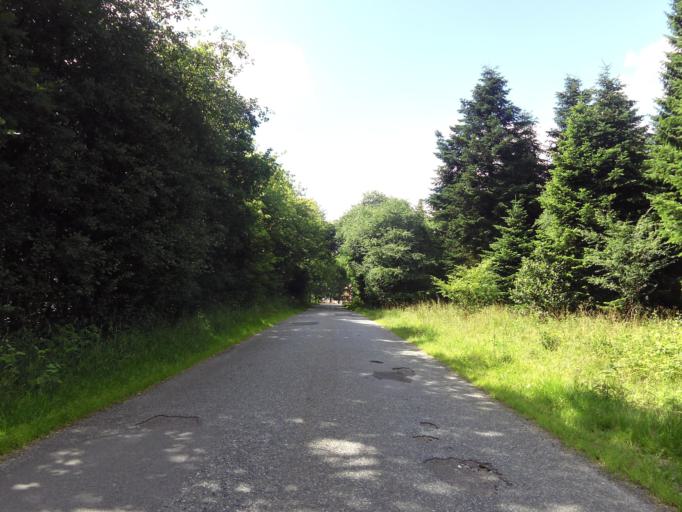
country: DK
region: South Denmark
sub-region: Haderslev Kommune
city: Vojens
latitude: 55.3147
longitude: 9.1980
